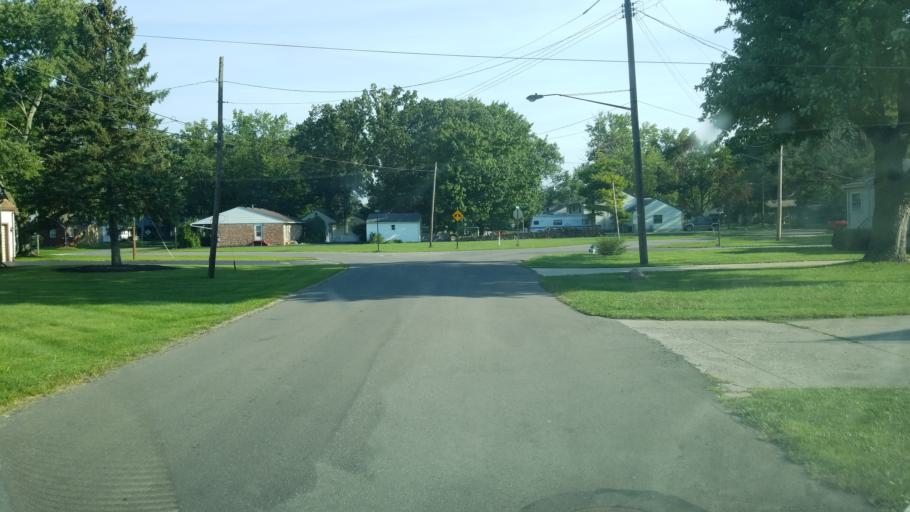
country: US
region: Ohio
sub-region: Marion County
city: Marion
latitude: 40.5830
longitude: -83.0995
